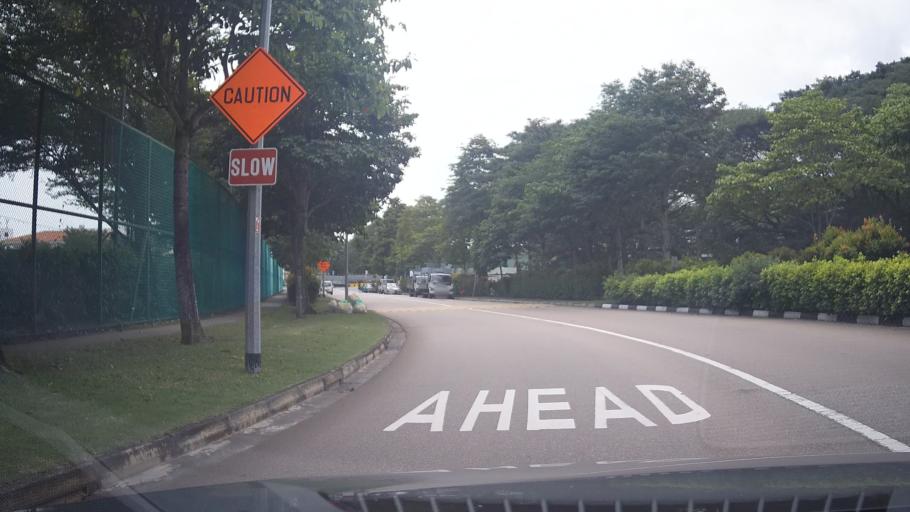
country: SG
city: Singapore
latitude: 1.2994
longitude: 103.8808
